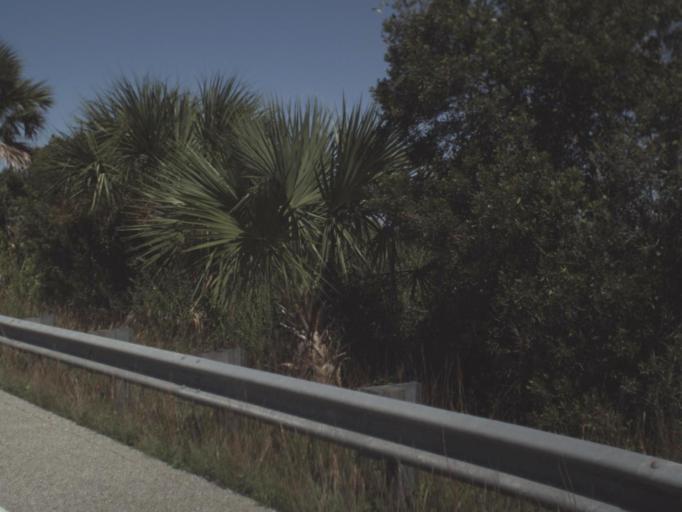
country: US
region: Florida
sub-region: Collier County
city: Marco
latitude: 25.9541
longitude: -81.4864
